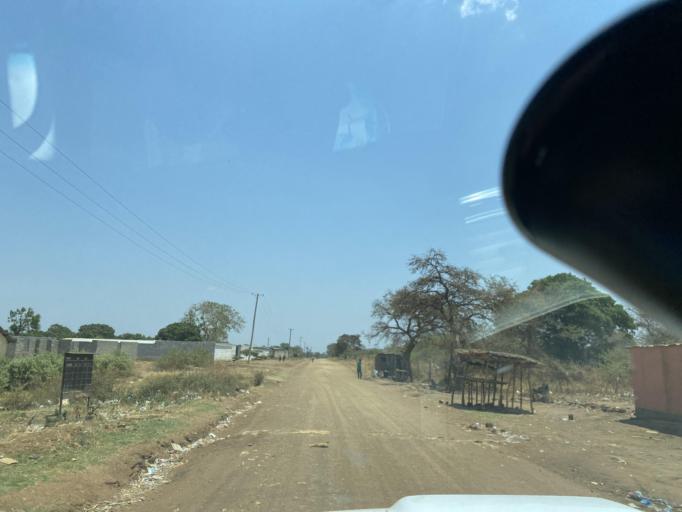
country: ZM
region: Lusaka
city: Lusaka
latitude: -15.4283
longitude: 28.0886
